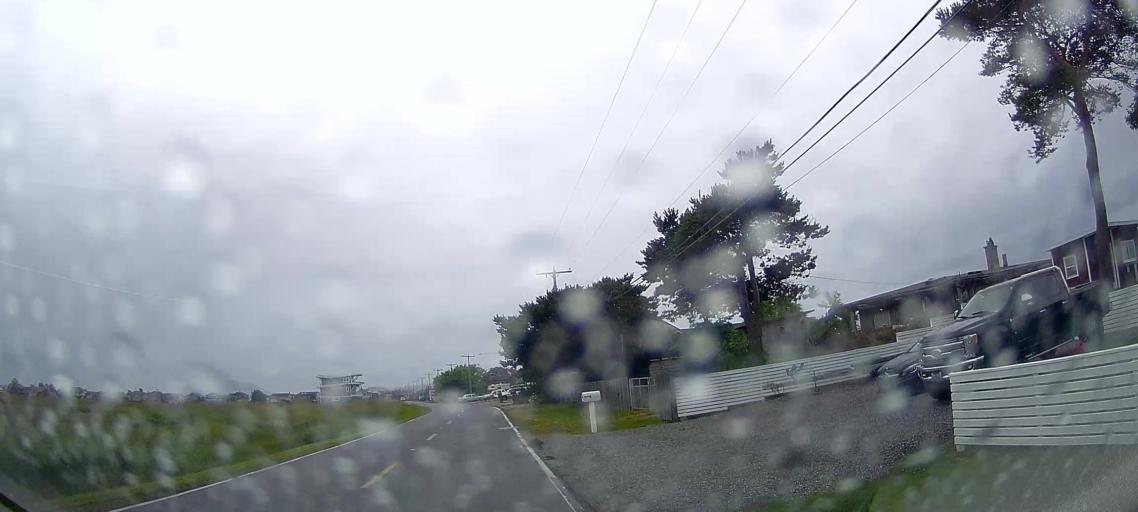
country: US
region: Washington
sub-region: Whatcom County
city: Birch Bay
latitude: 48.7947
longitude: -122.7104
